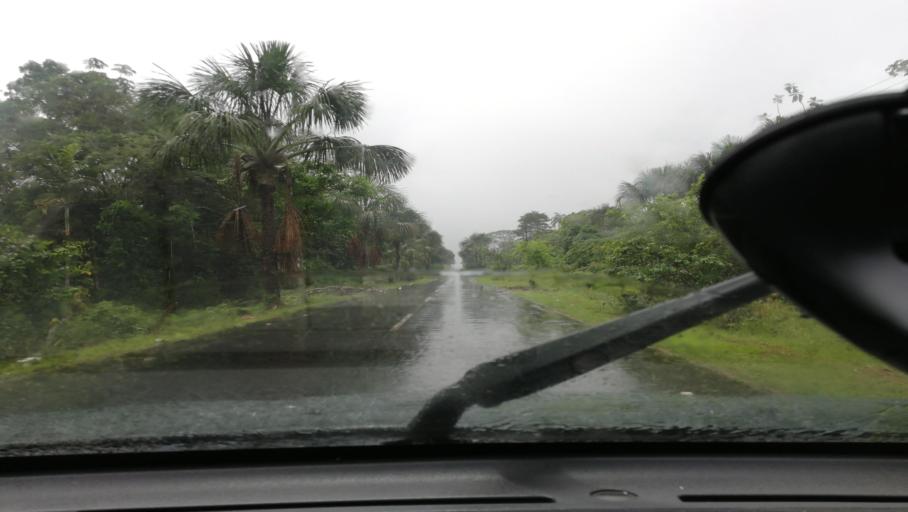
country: PE
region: Loreto
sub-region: Provincia de Maynas
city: San Juan
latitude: -3.9614
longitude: -73.4136
